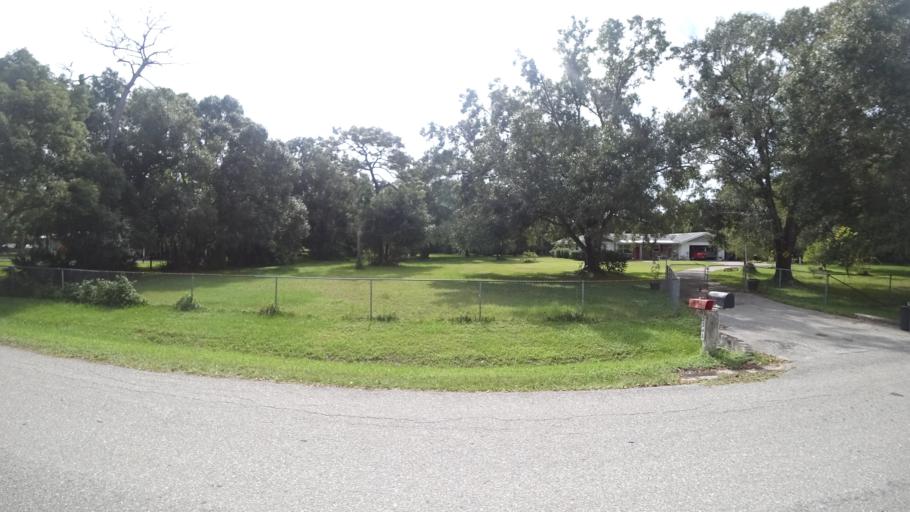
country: US
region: Florida
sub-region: Sarasota County
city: North Sarasota
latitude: 27.3870
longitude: -82.5244
